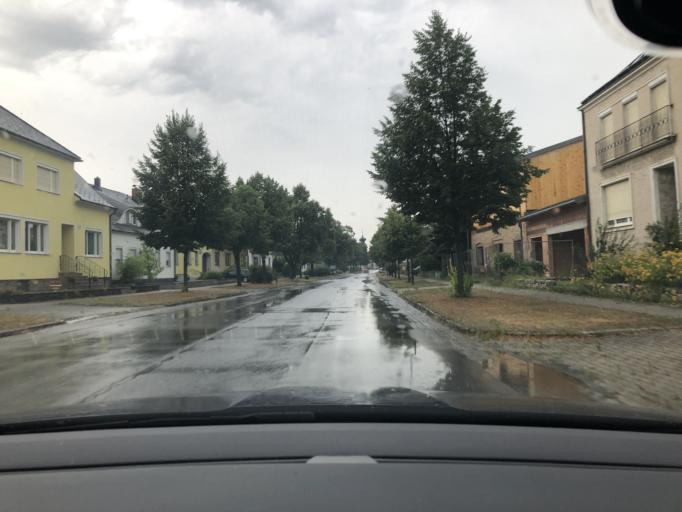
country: AT
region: Lower Austria
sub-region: Politischer Bezirk Ganserndorf
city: Angern an der March
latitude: 48.3078
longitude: 16.8277
